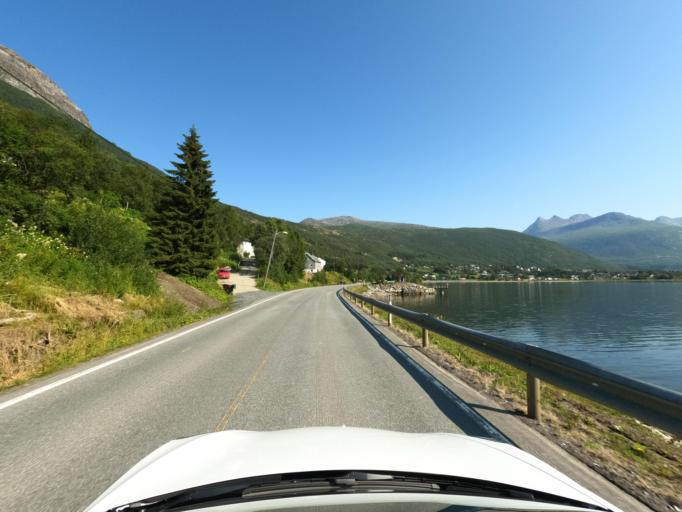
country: NO
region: Nordland
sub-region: Narvik
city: Narvik
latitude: 68.3830
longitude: 17.5841
